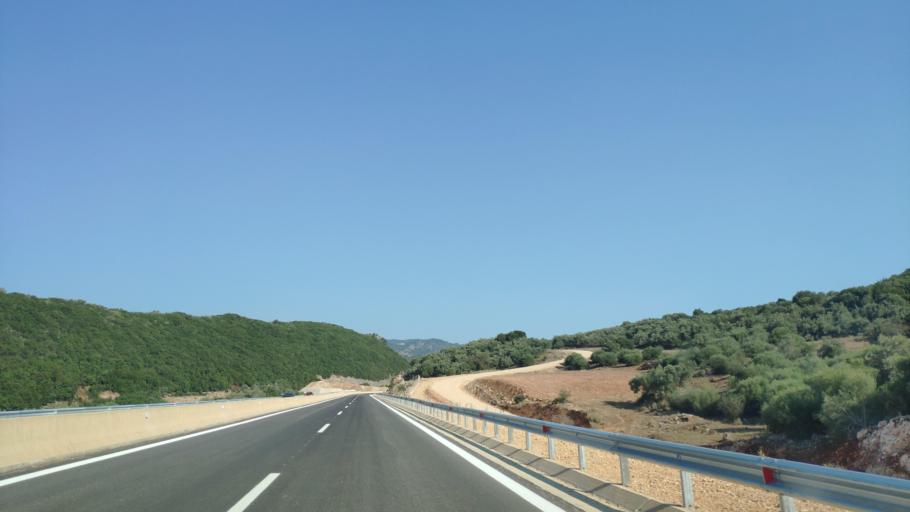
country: GR
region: West Greece
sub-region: Nomos Aitolias kai Akarnanias
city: Stanos
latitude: 38.7793
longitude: 21.1495
